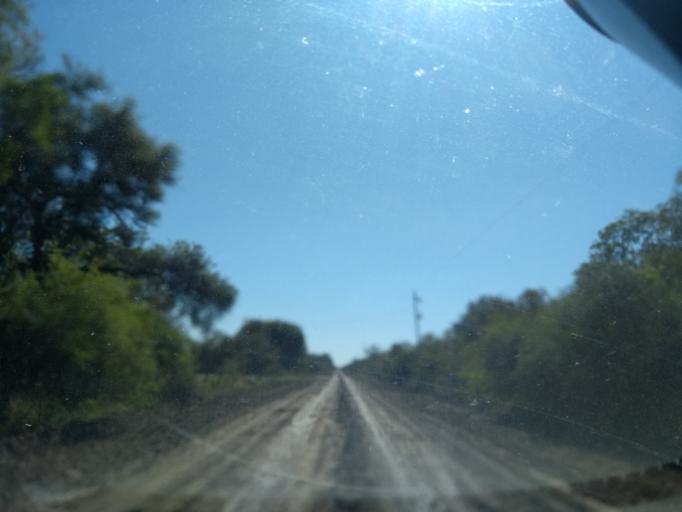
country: AR
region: Chaco
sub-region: Departamento de Quitilipi
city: Quitilipi
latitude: -26.7540
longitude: -60.2419
